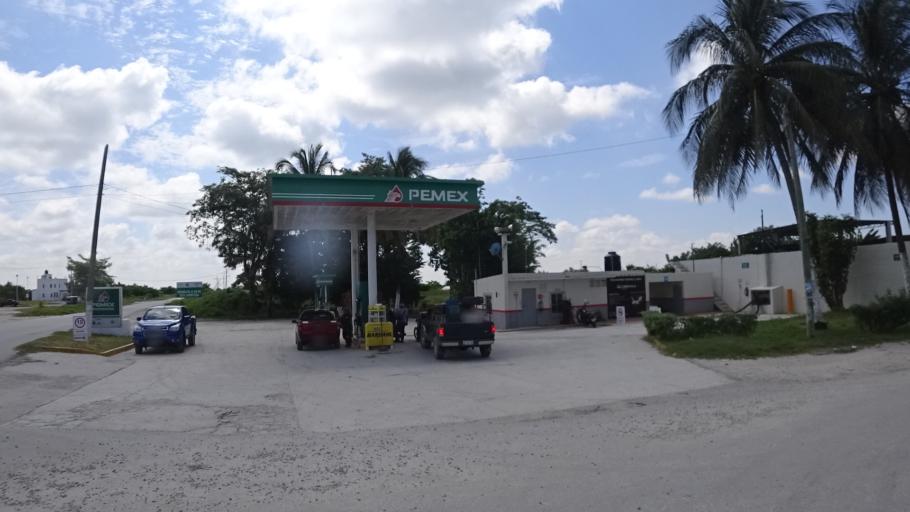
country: MX
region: Campeche
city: Sabancuy
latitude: 18.9684
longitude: -91.1763
